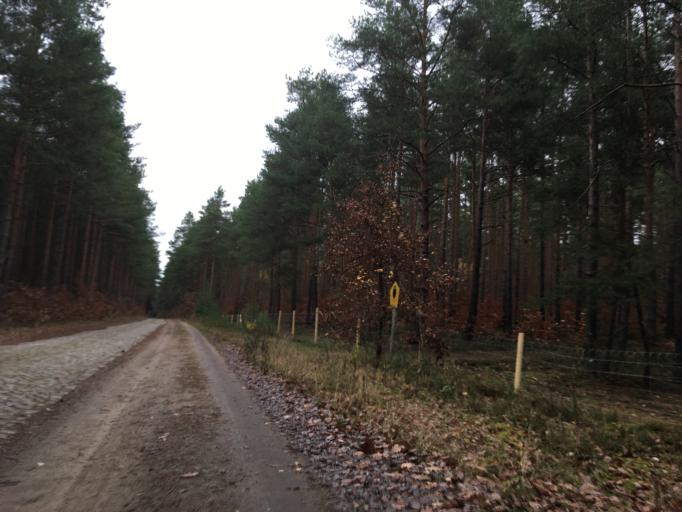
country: DE
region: Brandenburg
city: Jamlitz
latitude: 52.0647
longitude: 14.4825
